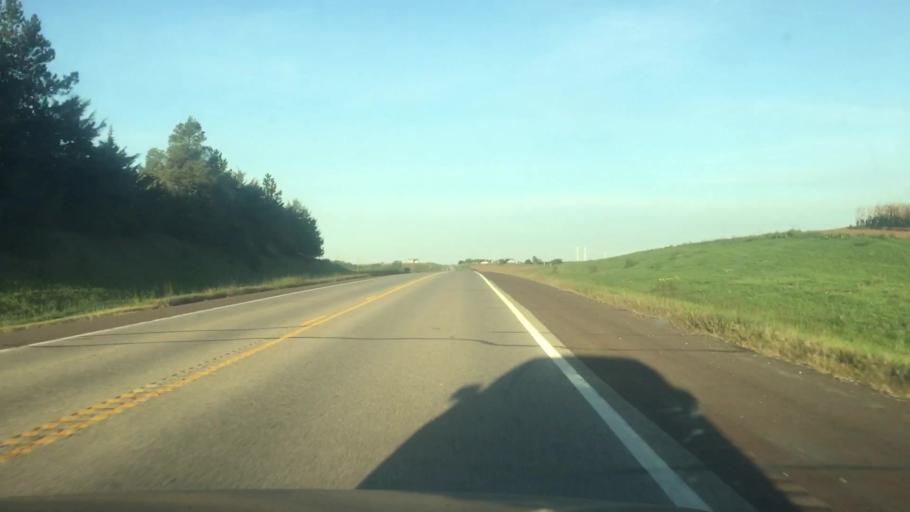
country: US
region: Kansas
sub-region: Nemaha County
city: Seneca
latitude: 39.8421
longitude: -96.2964
